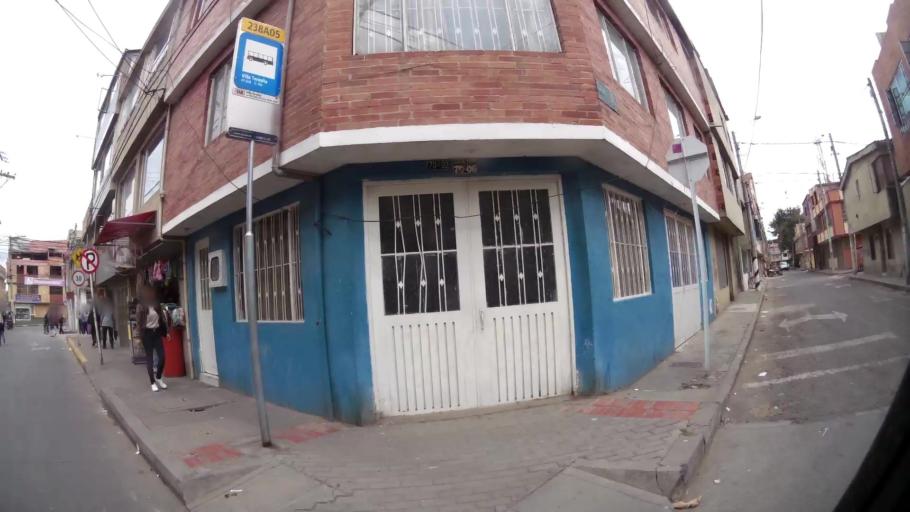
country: CO
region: Cundinamarca
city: Funza
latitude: 4.7141
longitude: -74.1351
